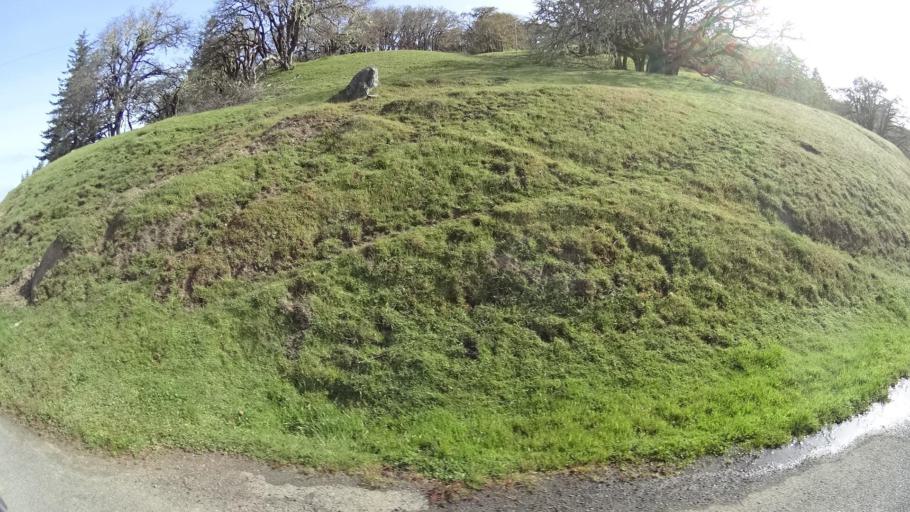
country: US
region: California
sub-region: Humboldt County
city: Hydesville
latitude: 40.6438
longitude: -123.9202
